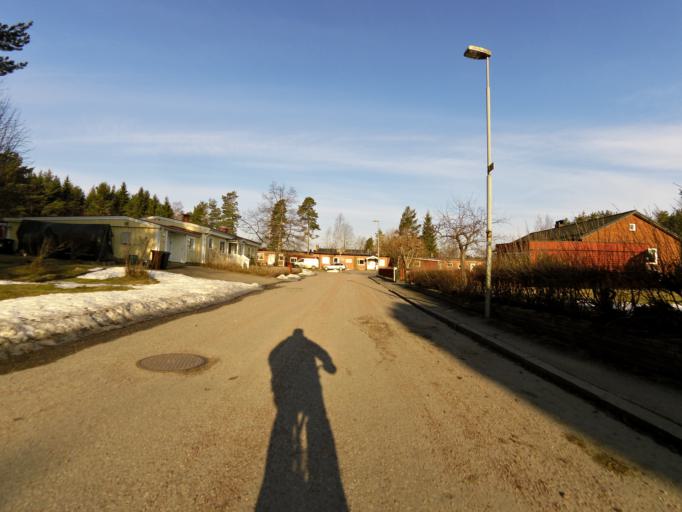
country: SE
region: Gaevleborg
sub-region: Gavle Kommun
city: Gavle
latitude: 60.6519
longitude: 17.1257
